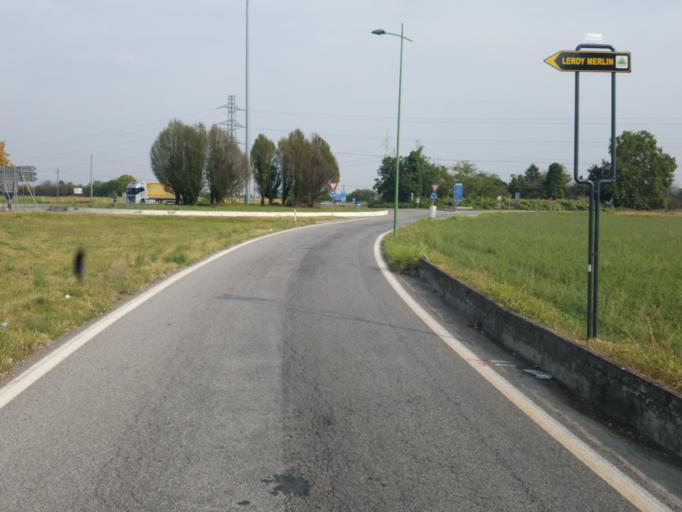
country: IT
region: Lombardy
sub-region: Provincia di Bergamo
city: Cavernago
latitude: 45.6424
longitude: 9.7514
